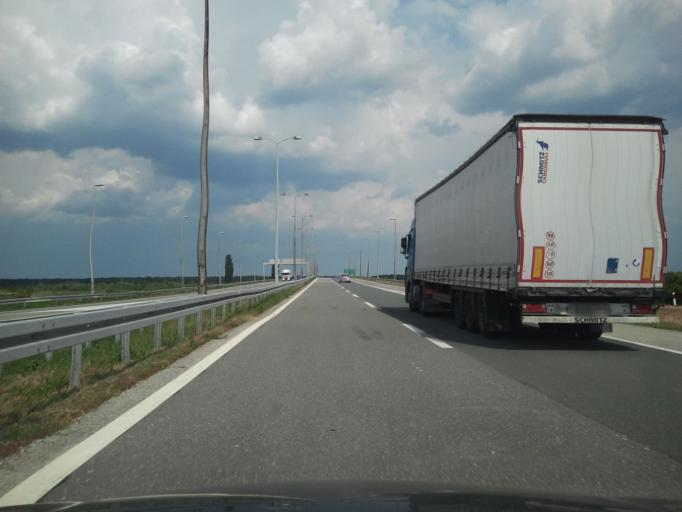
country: RS
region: Autonomna Pokrajina Vojvodina
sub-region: Sremski Okrug
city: Sid
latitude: 45.0481
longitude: 19.2058
